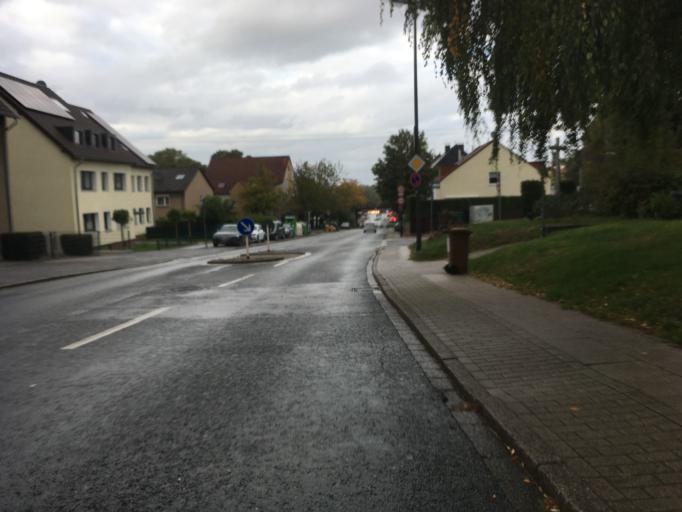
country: DE
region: North Rhine-Westphalia
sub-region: Regierungsbezirk Munster
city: Bottrop
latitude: 51.4846
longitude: 6.9324
